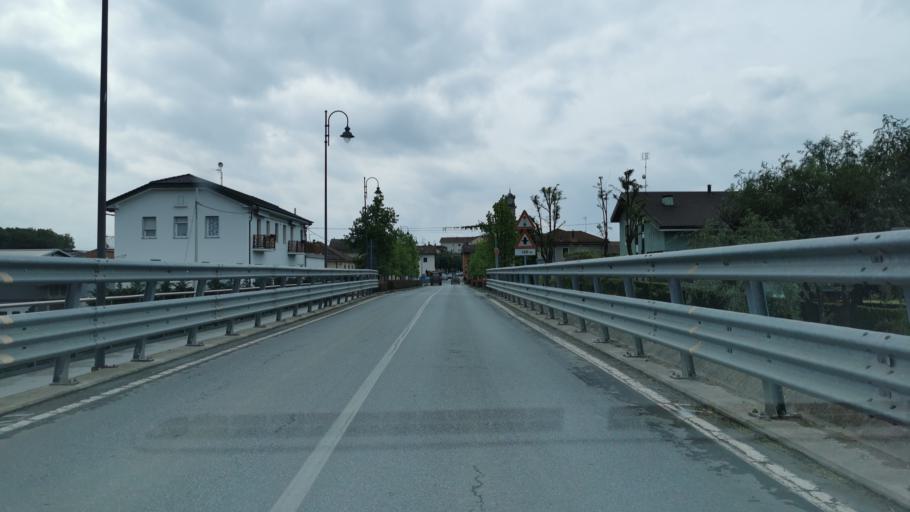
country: IT
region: Piedmont
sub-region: Provincia di Cuneo
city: Villafalletto
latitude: 44.5482
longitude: 7.5386
